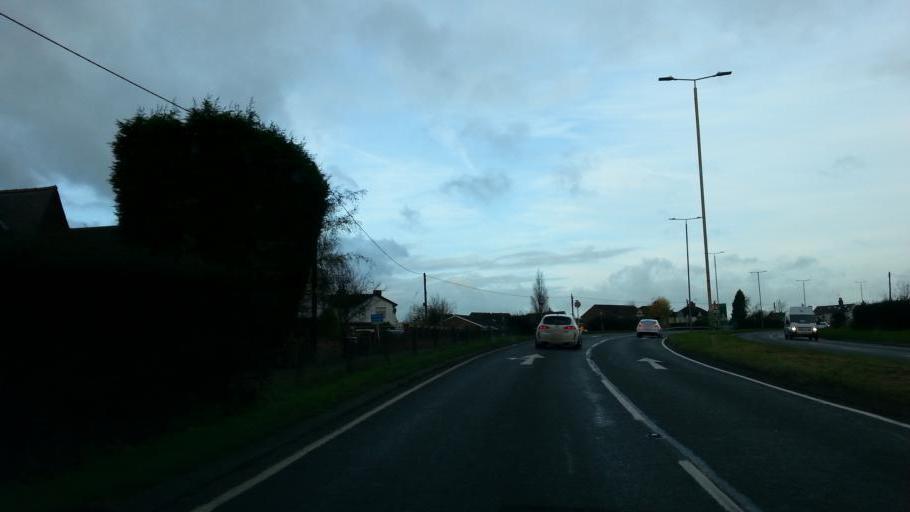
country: GB
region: England
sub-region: Leicestershire
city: Markfield
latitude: 52.6835
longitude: -1.2649
